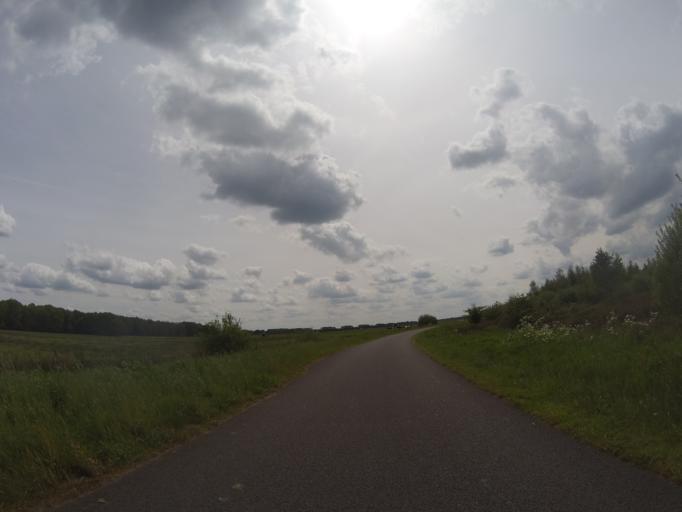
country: NL
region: Drenthe
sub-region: Gemeente Assen
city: Assen
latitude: 52.9028
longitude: 6.6320
